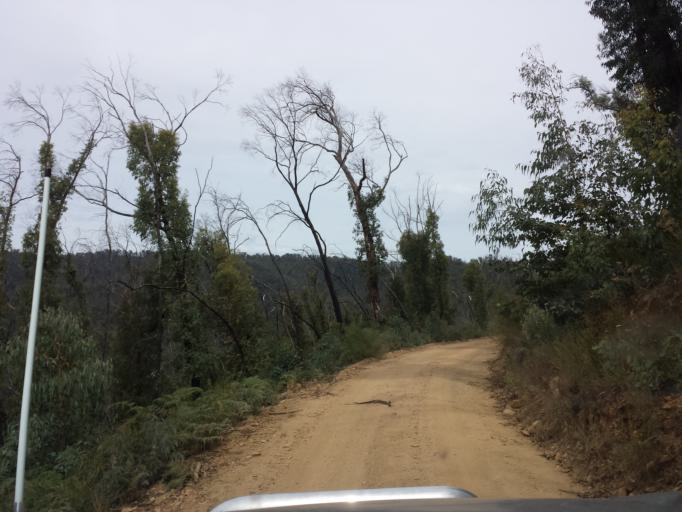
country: AU
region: Victoria
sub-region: Wellington
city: Heyfield
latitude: -37.7442
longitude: 146.4063
